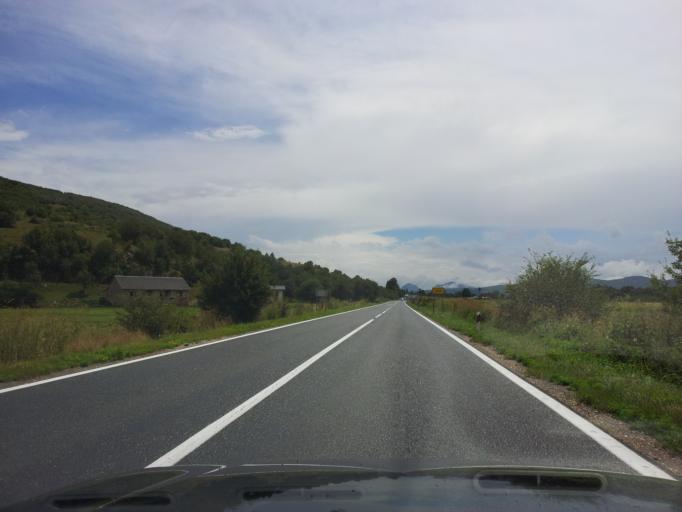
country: BA
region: Federation of Bosnia and Herzegovina
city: Bihac
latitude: 44.6065
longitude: 15.7364
